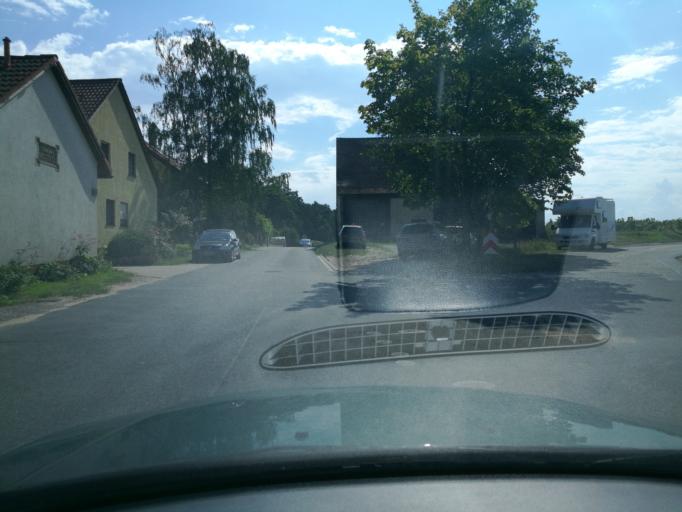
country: DE
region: Bavaria
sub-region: Regierungsbezirk Mittelfranken
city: Furth
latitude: 49.5107
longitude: 10.9541
